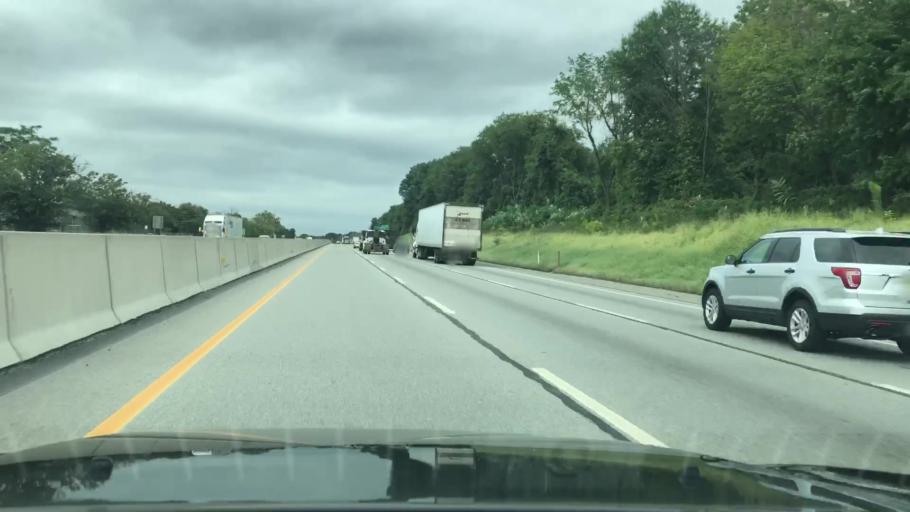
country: US
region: Pennsylvania
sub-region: Montgomery County
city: Hatboro
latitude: 40.1624
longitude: -75.0949
